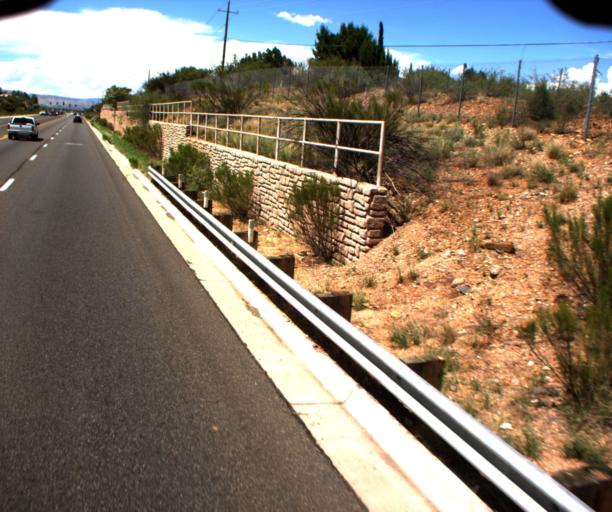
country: US
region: Arizona
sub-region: Yavapai County
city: Verde Village
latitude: 34.6961
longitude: -111.9851
